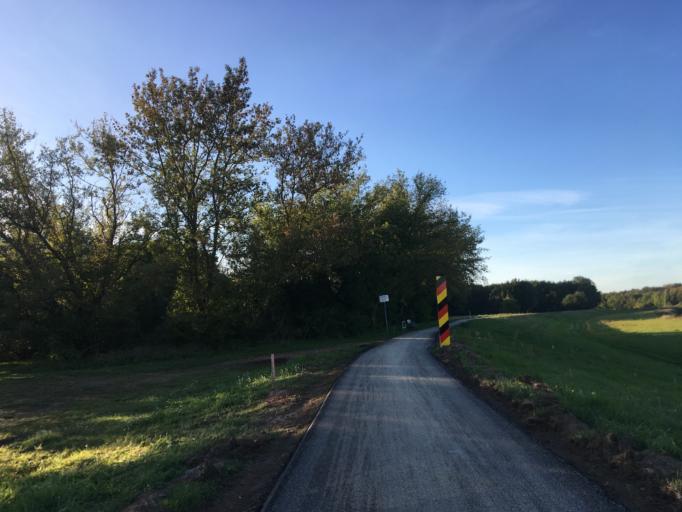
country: DE
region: Brandenburg
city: Forst
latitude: 51.7167
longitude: 14.6799
